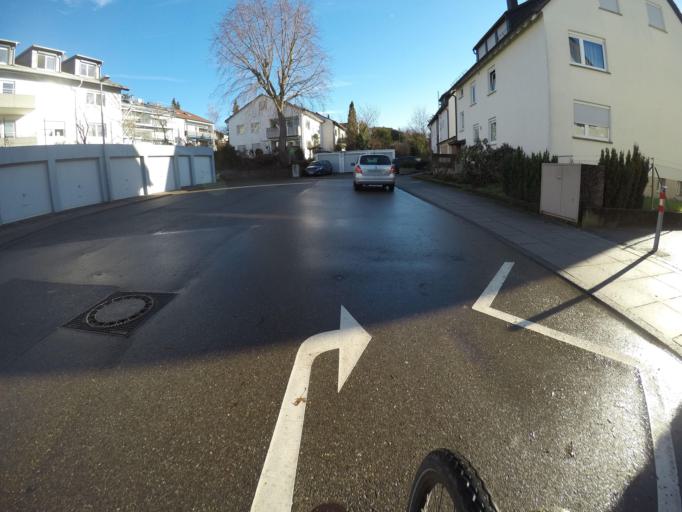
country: DE
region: Baden-Wuerttemberg
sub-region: Regierungsbezirk Stuttgart
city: Fellbach
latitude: 48.8038
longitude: 9.2439
